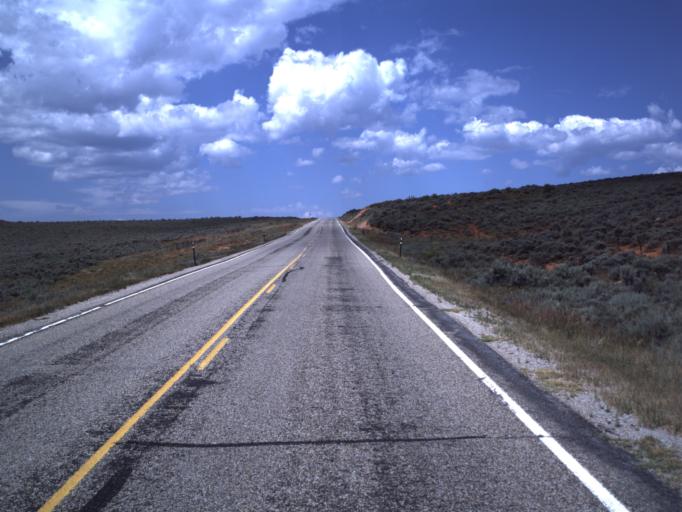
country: US
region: Utah
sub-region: Rich County
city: Randolph
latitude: 41.7965
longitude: -111.2347
